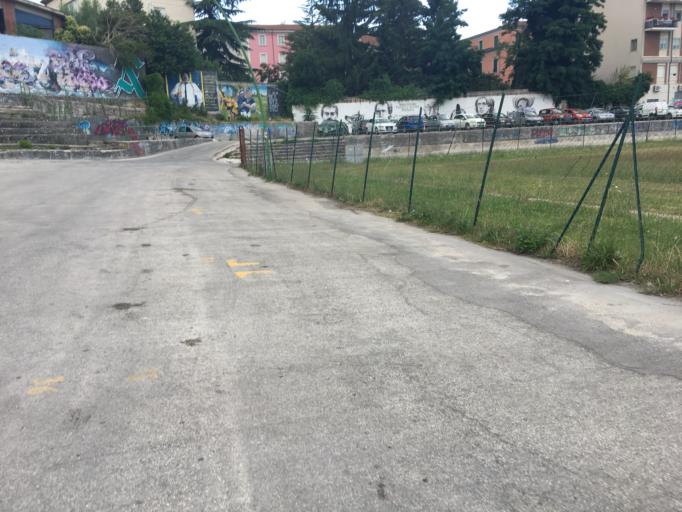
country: IT
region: Molise
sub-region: Provincia di Campobasso
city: Campobasso
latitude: 41.5547
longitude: 14.6595
